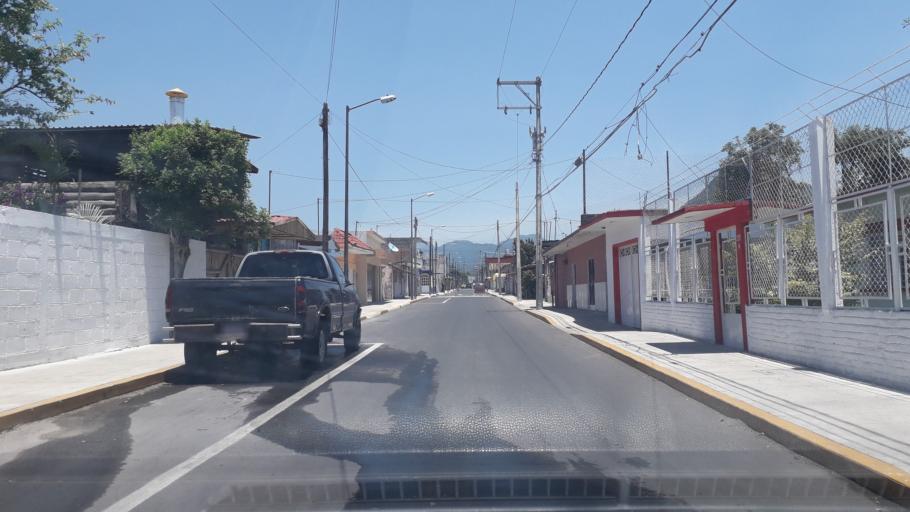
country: MX
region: Veracruz
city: Jalapilla
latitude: 18.8387
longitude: -97.0896
